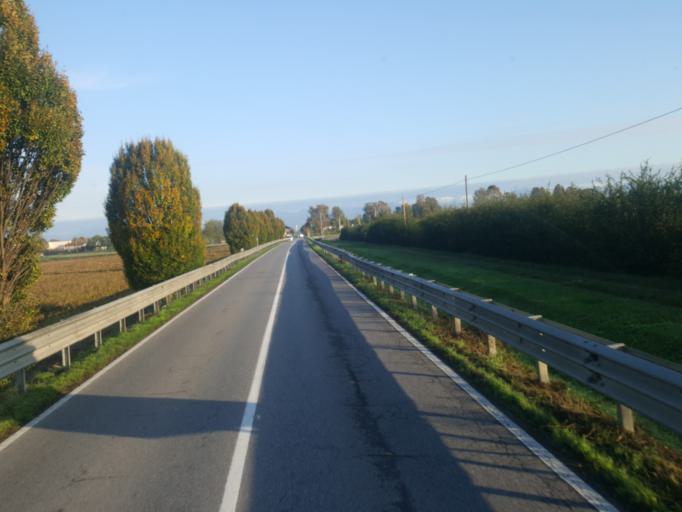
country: IT
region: Lombardy
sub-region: Provincia di Bergamo
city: Morengo
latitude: 45.5497
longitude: 9.7065
